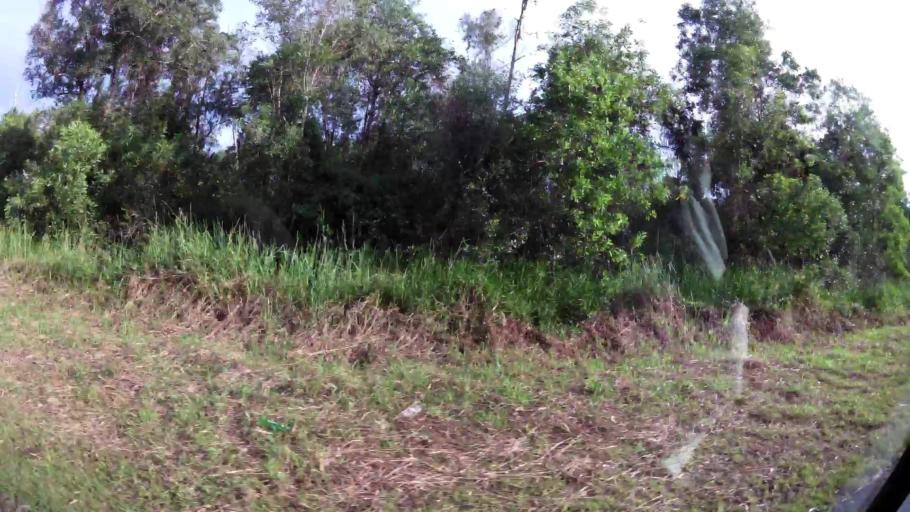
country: BN
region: Brunei and Muara
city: Bandar Seri Begawan
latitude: 4.9620
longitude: 115.0262
